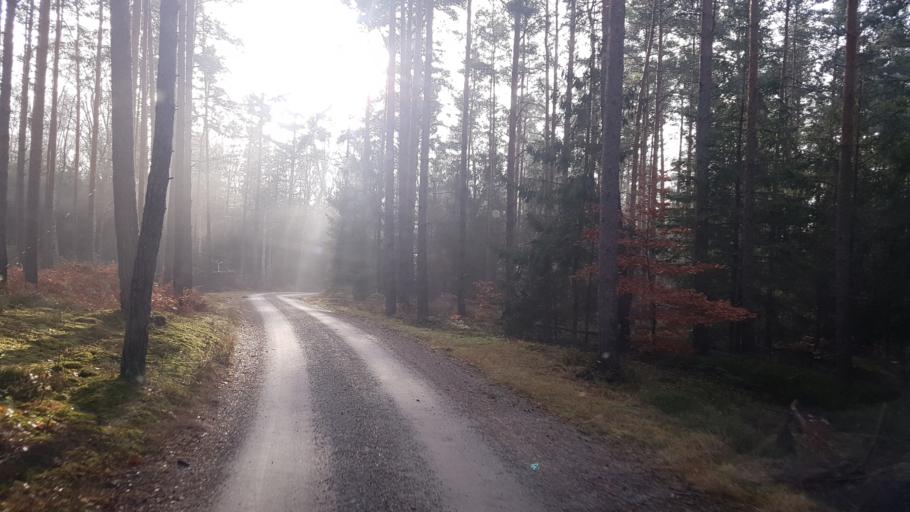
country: DE
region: Brandenburg
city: Schonborn
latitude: 51.6244
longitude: 13.5088
